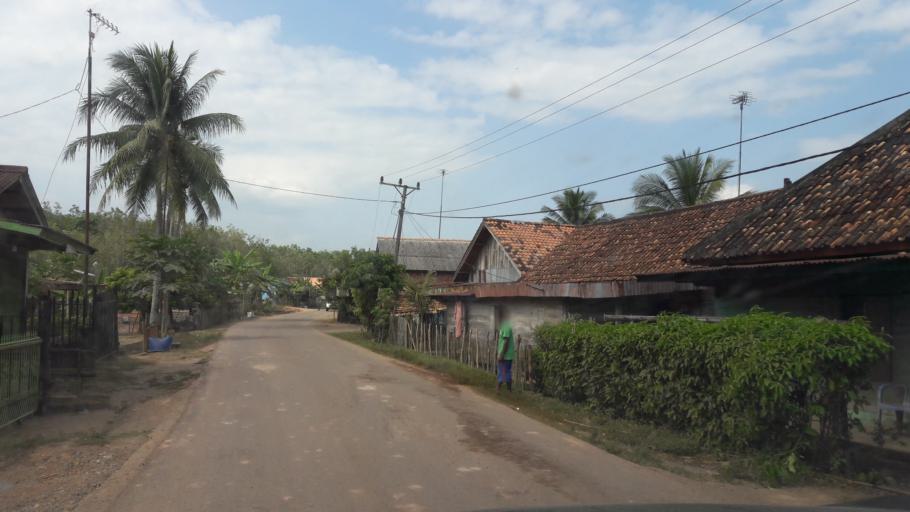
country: ID
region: South Sumatra
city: Prabumulih
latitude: -3.3242
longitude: 104.1271
